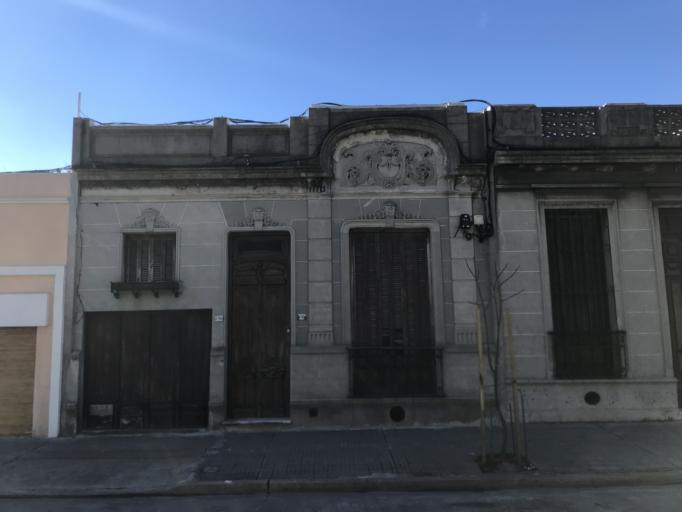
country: UY
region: Montevideo
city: Montevideo
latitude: -34.8969
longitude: -56.1784
